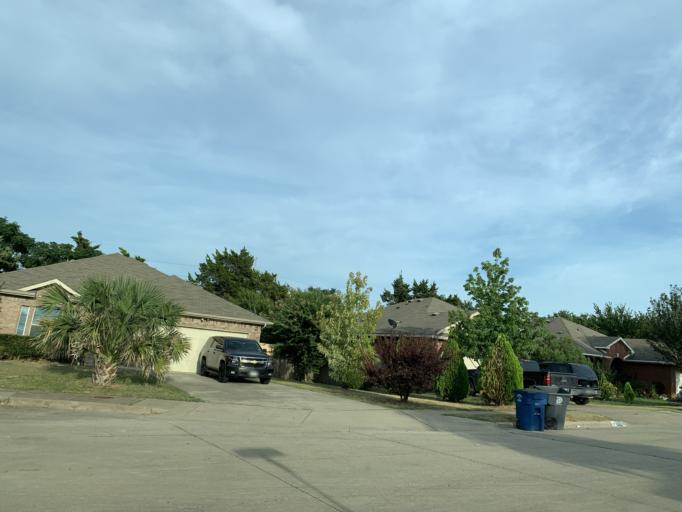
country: US
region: Texas
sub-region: Dallas County
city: Cockrell Hill
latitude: 32.6998
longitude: -96.8924
